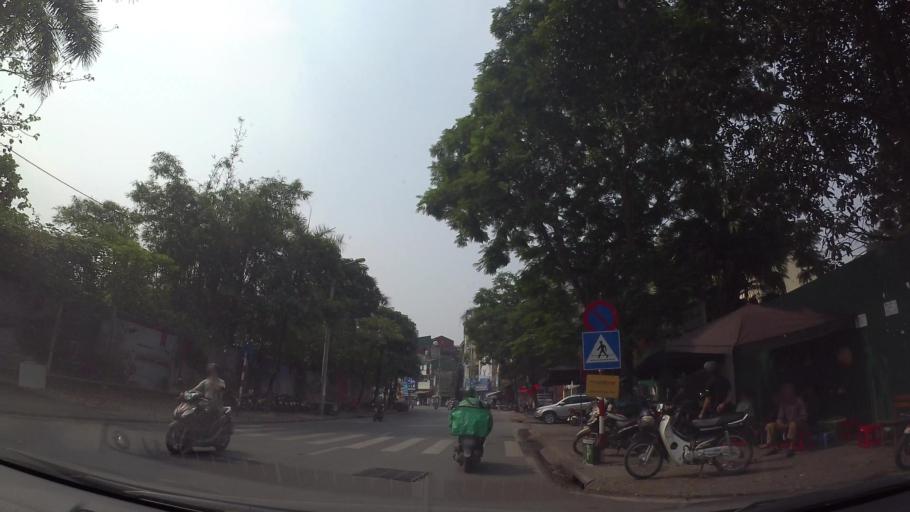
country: VN
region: Ha Noi
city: Dong Da
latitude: 21.0269
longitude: 105.8178
